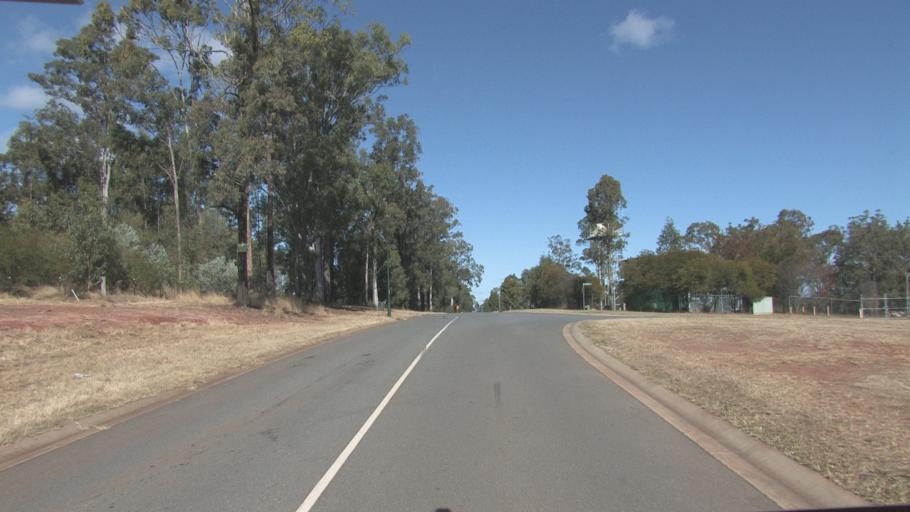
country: AU
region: Queensland
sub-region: Logan
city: Cedar Vale
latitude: -27.8919
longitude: 153.0024
